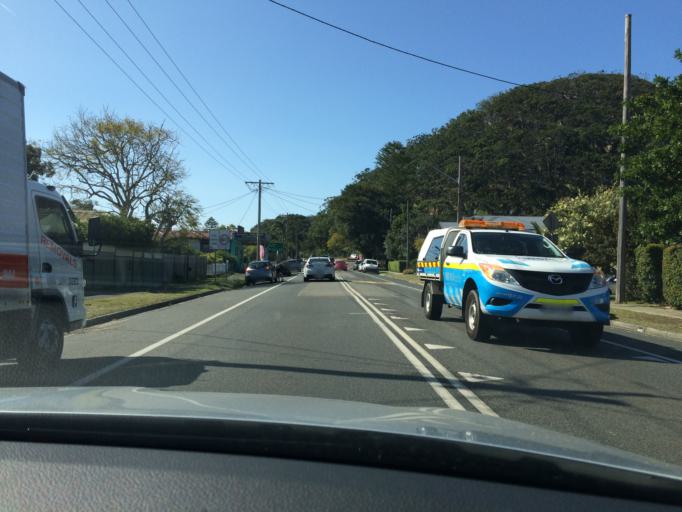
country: AU
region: New South Wales
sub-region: Gosford Shire
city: Ettalong Beach
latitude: -33.5111
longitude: 151.3306
